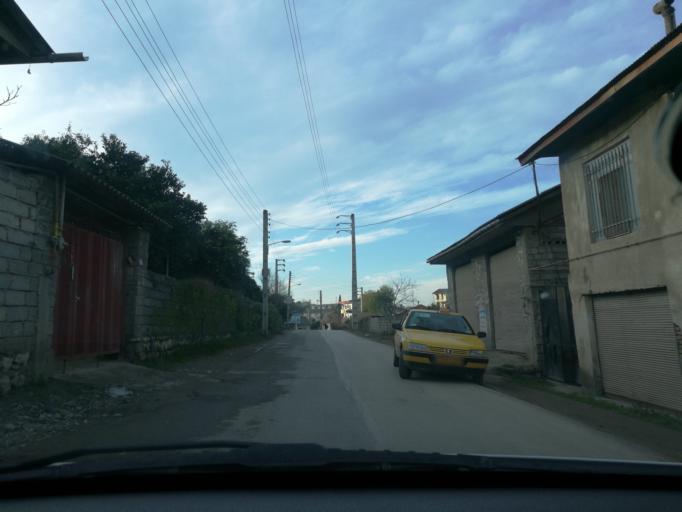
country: IR
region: Mazandaran
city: Chalus
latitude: 36.6414
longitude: 51.4405
